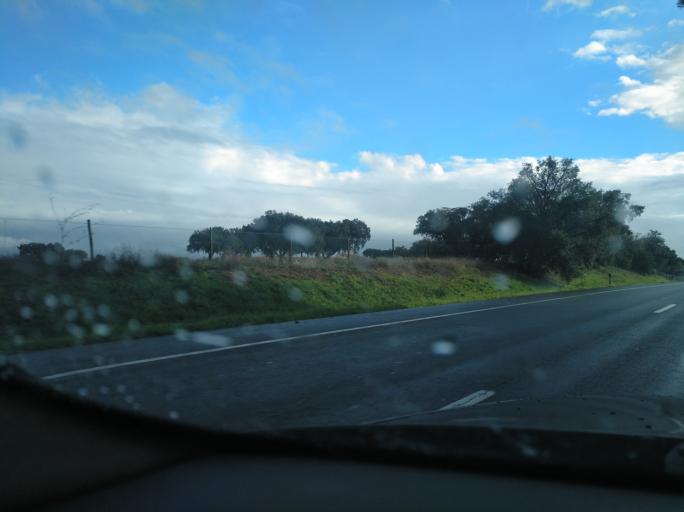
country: PT
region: Setubal
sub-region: Grandola
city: Grandola
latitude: 38.0390
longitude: -8.4010
